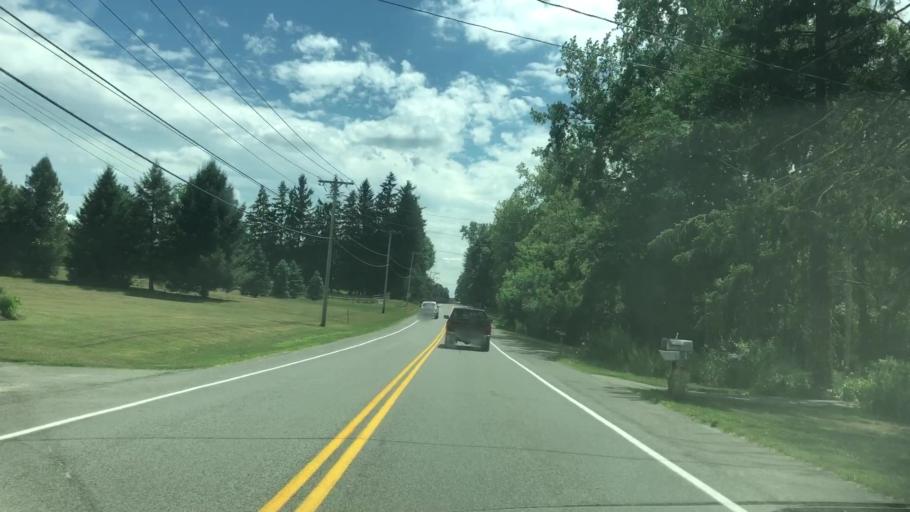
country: US
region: New York
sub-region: Monroe County
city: Fairport
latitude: 43.1353
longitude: -77.4006
